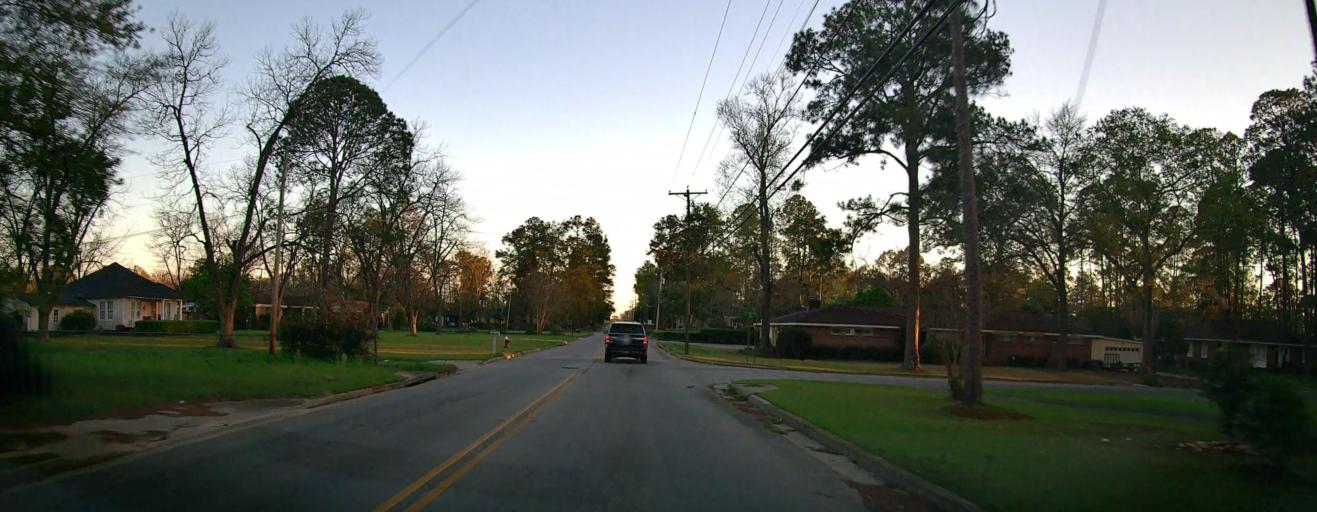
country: US
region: Georgia
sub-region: Crisp County
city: Cordele
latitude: 31.9589
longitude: -83.7655
